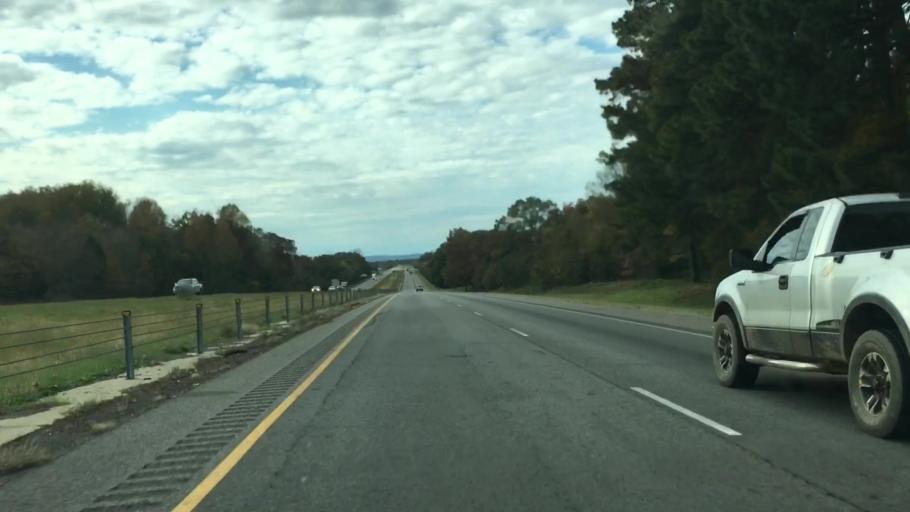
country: US
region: Arkansas
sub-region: Conway County
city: Morrilton
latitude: 35.1810
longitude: -92.7603
